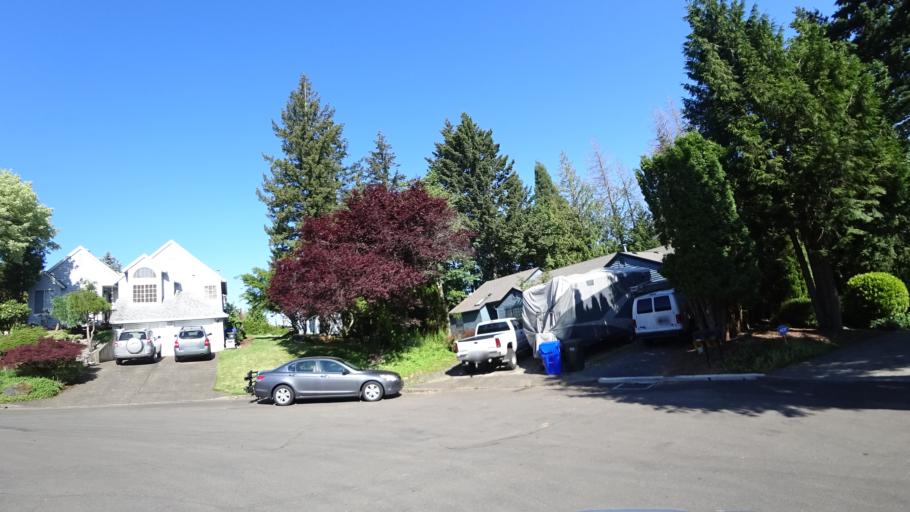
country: US
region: Oregon
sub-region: Multnomah County
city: Lents
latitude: 45.4674
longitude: -122.5456
